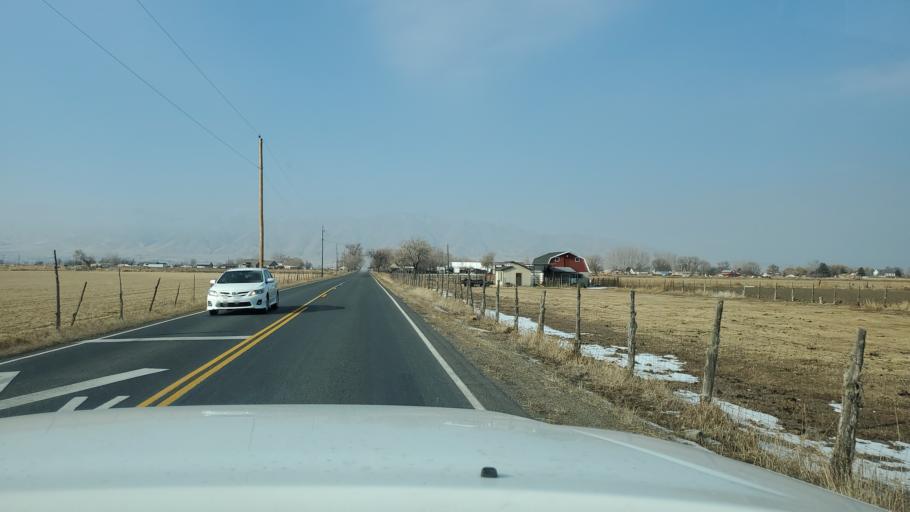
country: US
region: Utah
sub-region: Utah County
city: Benjamin
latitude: 40.0853
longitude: -111.7213
